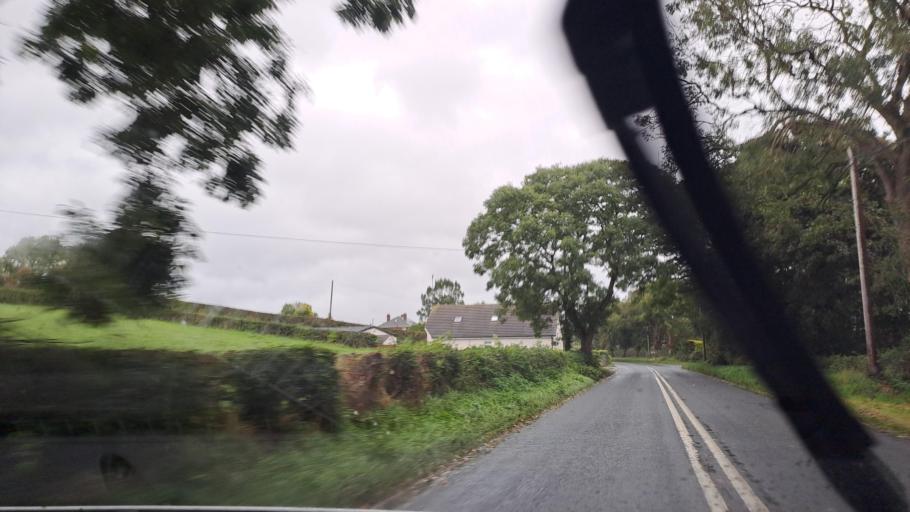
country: IE
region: Leinster
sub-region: Lu
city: Dundalk
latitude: 53.9792
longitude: -6.5117
